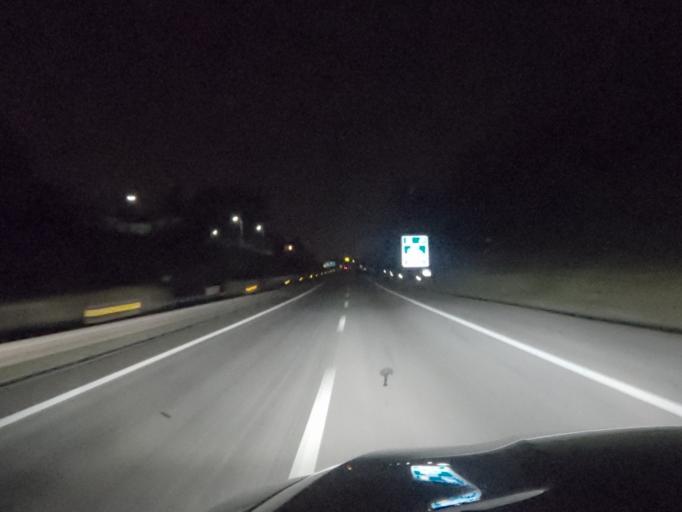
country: PT
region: Porto
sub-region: Vila Nova de Gaia
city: Oliveira do Douro
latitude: 41.1210
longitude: -8.5725
